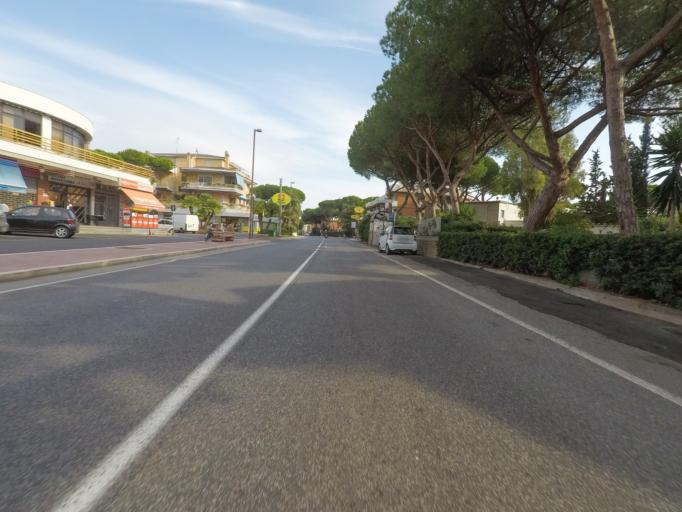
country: IT
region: Latium
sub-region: Citta metropolitana di Roma Capitale
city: Santa Marinella
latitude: 42.0332
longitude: 11.8373
